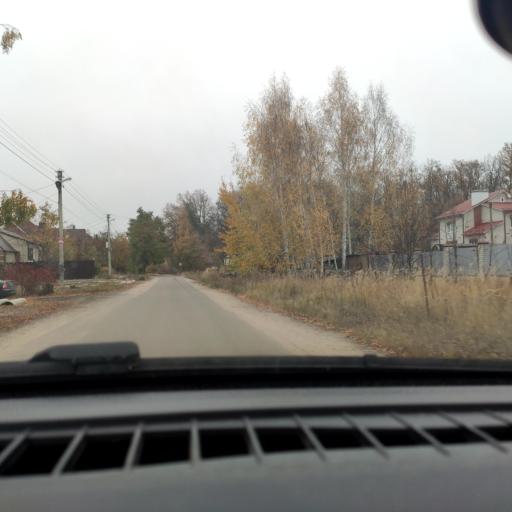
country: RU
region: Voronezj
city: Podgornoye
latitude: 51.7659
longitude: 39.1824
